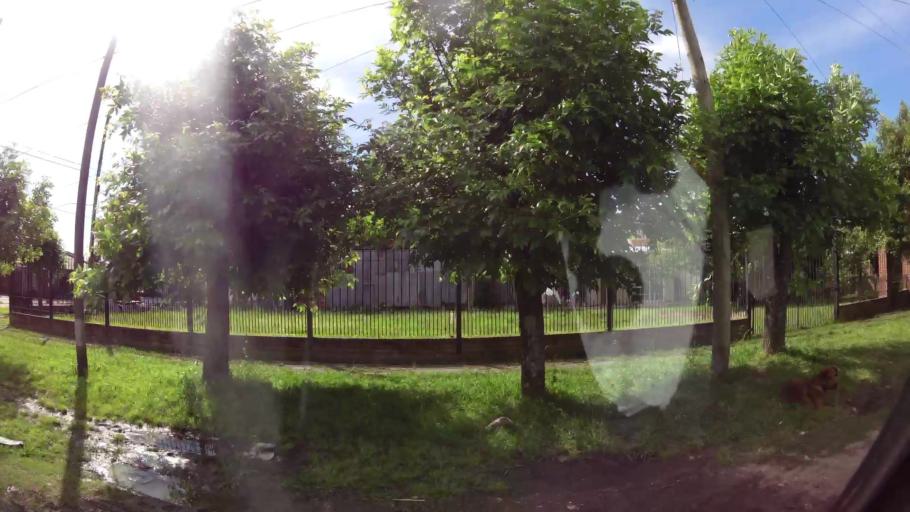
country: AR
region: Buenos Aires
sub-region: Partido de Almirante Brown
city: Adrogue
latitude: -34.8120
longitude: -58.3549
